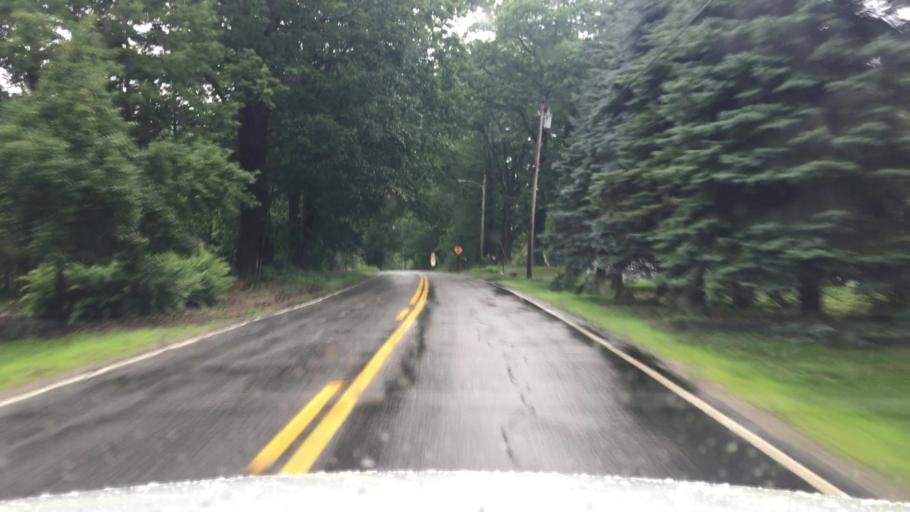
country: US
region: Maine
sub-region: Kennebec County
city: Winthrop
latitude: 44.3166
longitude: -69.9248
